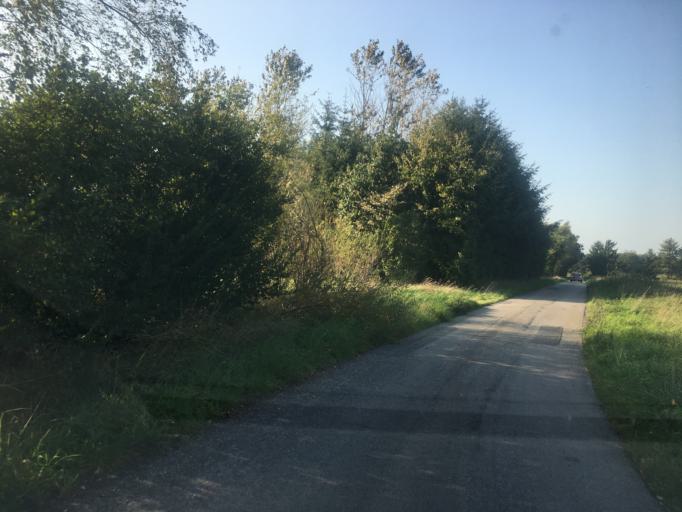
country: DE
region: Schleswig-Holstein
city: Ellhoft
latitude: 54.9268
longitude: 9.0107
